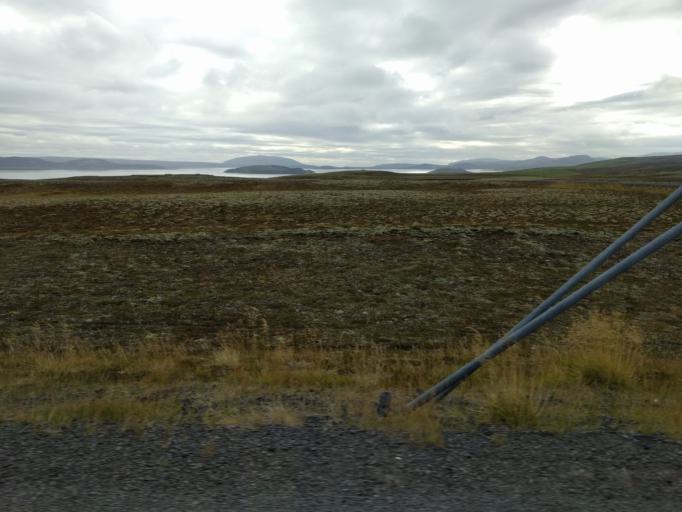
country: IS
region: South
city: Hveragerdi
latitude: 64.2159
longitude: -21.2451
